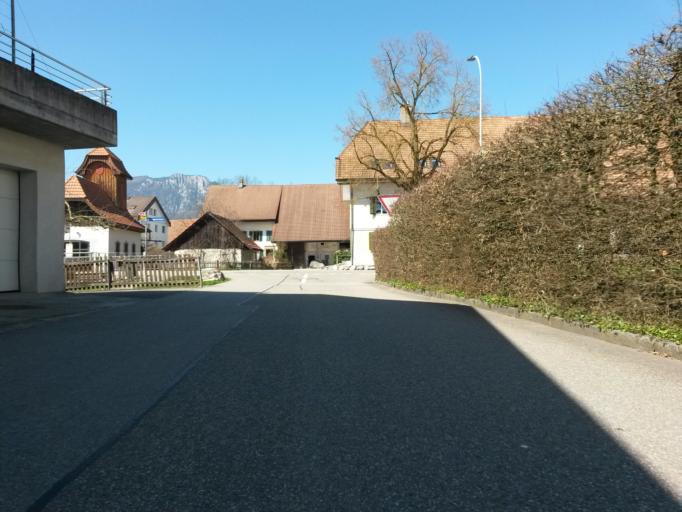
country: CH
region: Solothurn
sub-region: Bezirk Wasseramt
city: Luterbach
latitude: 47.2160
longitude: 7.5886
